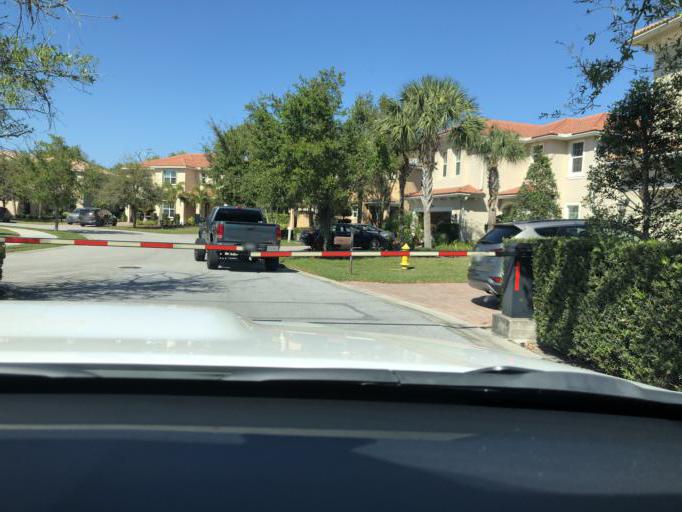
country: US
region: Florida
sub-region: Martin County
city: Palm City
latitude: 27.1686
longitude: -80.2738
